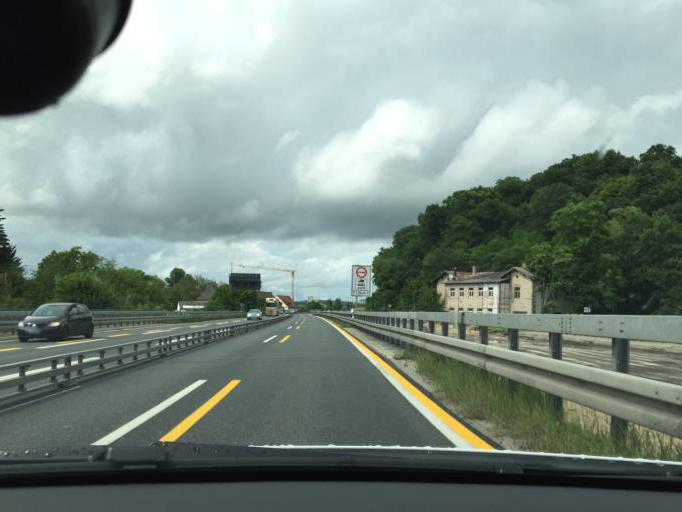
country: DE
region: Bavaria
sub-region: Regierungsbezirk Mittelfranken
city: Erlangen
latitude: 49.6080
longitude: 10.9985
